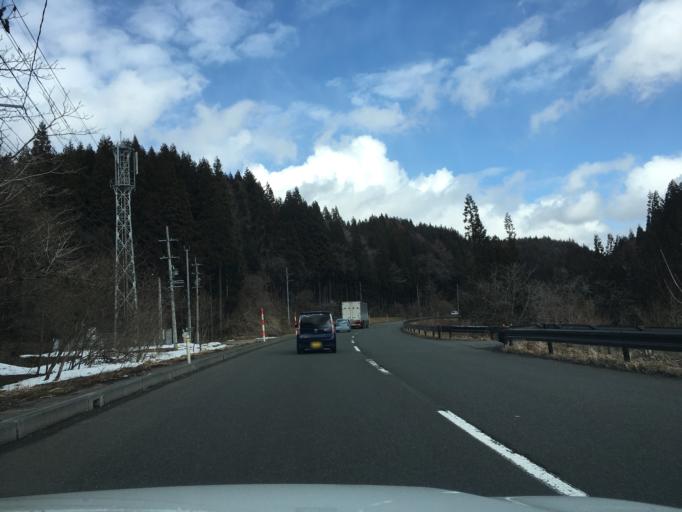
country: JP
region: Akita
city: Takanosu
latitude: 40.0972
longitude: 140.3412
